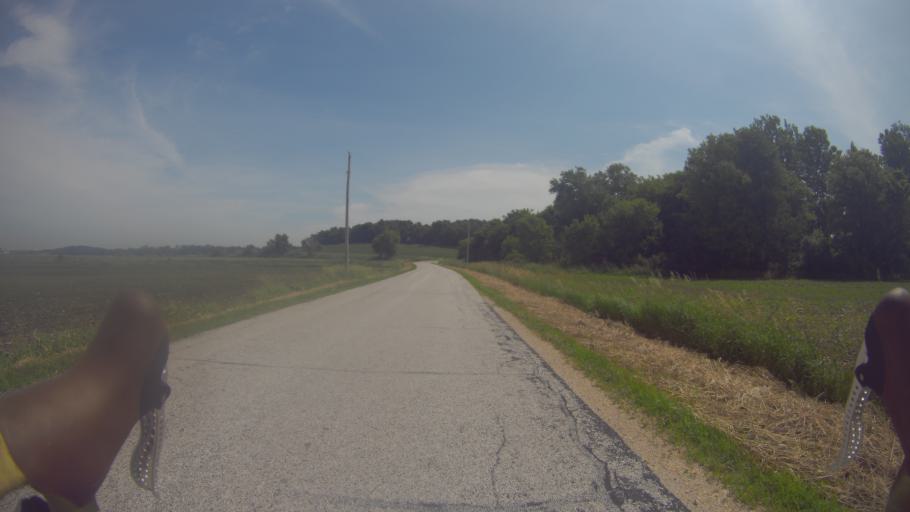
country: US
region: Wisconsin
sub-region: Dane County
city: Deerfield
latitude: 43.0570
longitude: -89.0277
